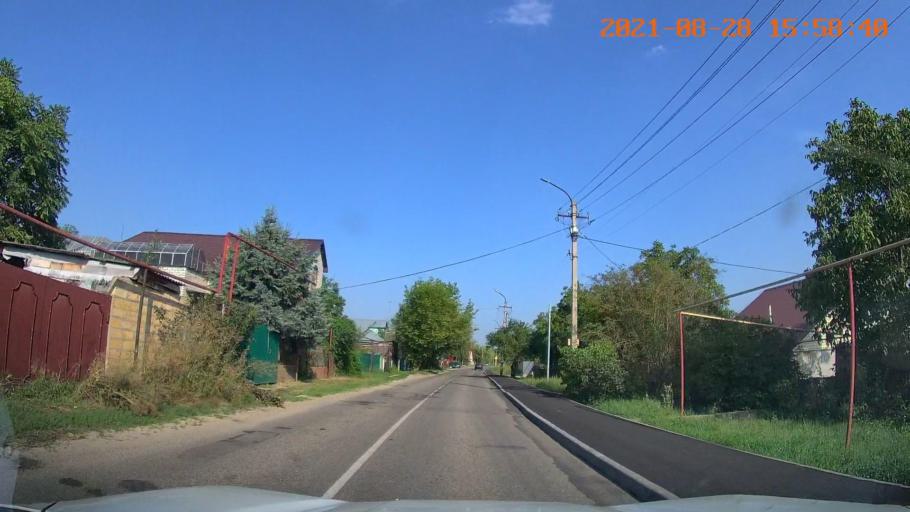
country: RU
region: Stavropol'skiy
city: Tatarka
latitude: 44.9617
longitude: 41.9549
